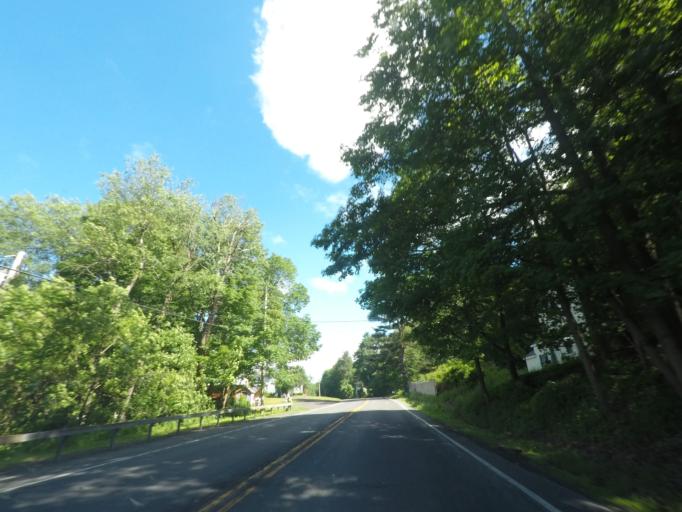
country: US
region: New York
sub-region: Columbia County
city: Philmont
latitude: 42.1917
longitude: -73.6216
